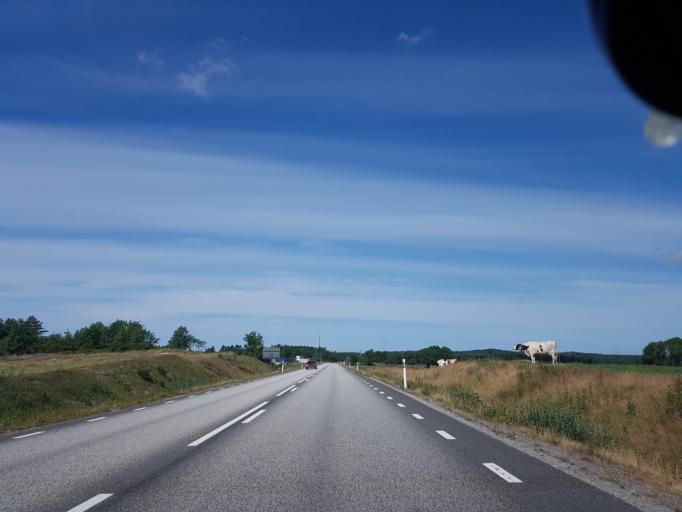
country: SE
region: Vaestra Goetaland
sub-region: Orust
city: Henan
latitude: 58.1506
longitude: 11.5843
